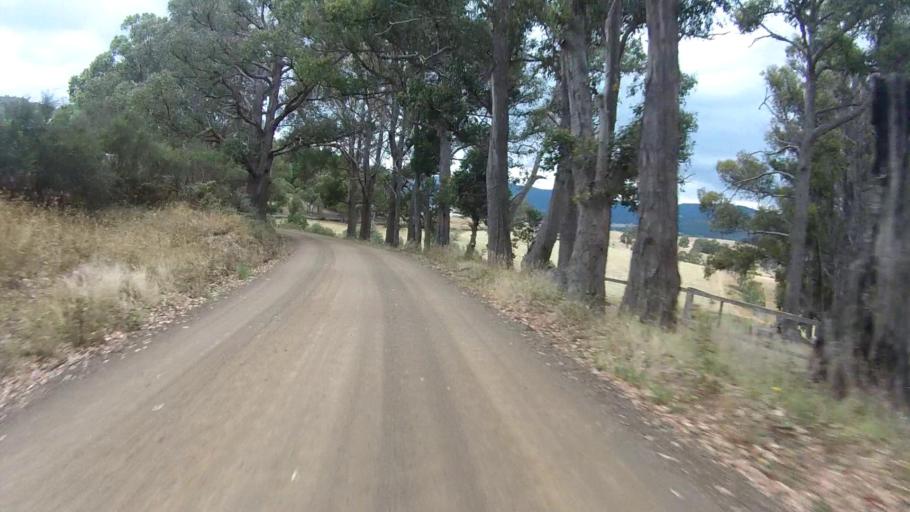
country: AU
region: Tasmania
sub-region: Huon Valley
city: Huonville
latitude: -42.9713
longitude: 147.0597
